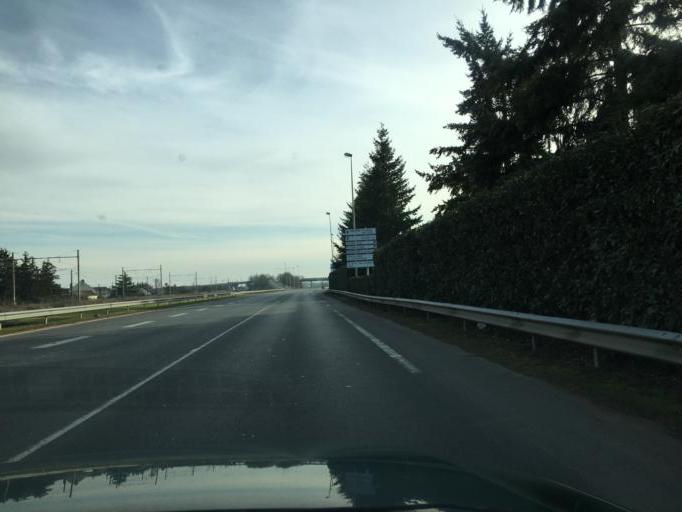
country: FR
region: Centre
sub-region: Departement du Loiret
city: Saint-Jean-le-Blanc
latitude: 47.8745
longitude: 1.9300
